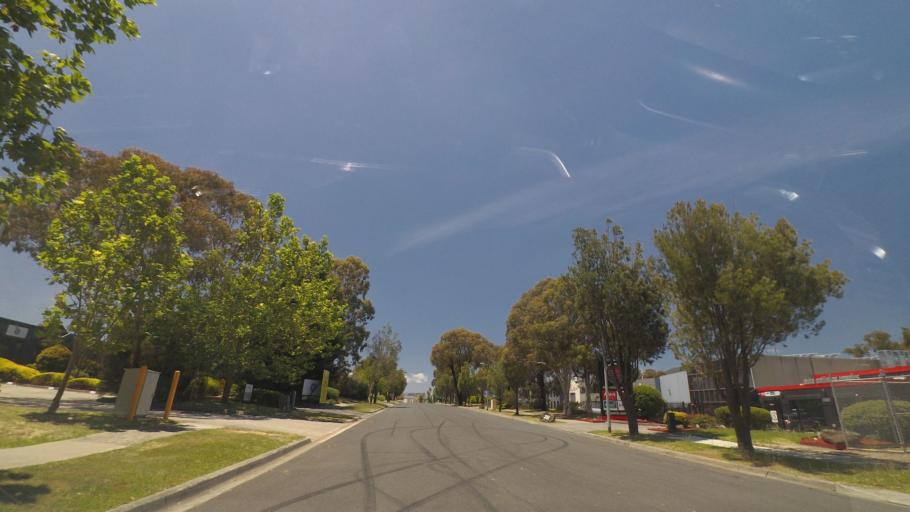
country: AU
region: Victoria
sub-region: Maroondah
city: Bayswater North
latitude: -37.8170
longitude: 145.2931
